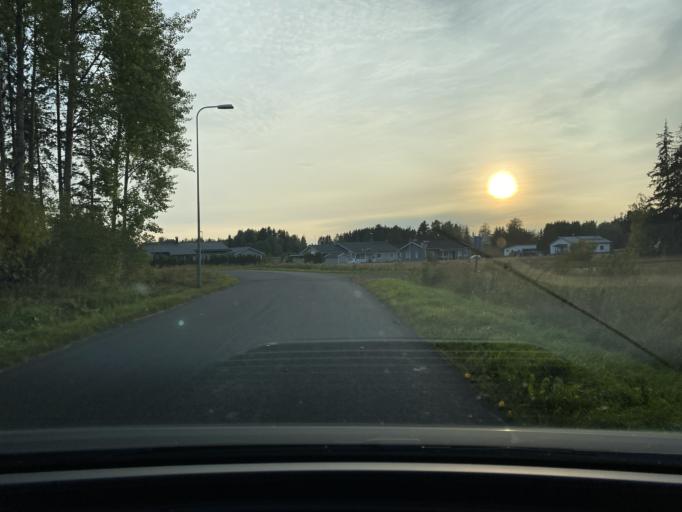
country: FI
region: Pirkanmaa
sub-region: Lounais-Pirkanmaa
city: Punkalaidun
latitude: 61.1227
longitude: 23.0861
